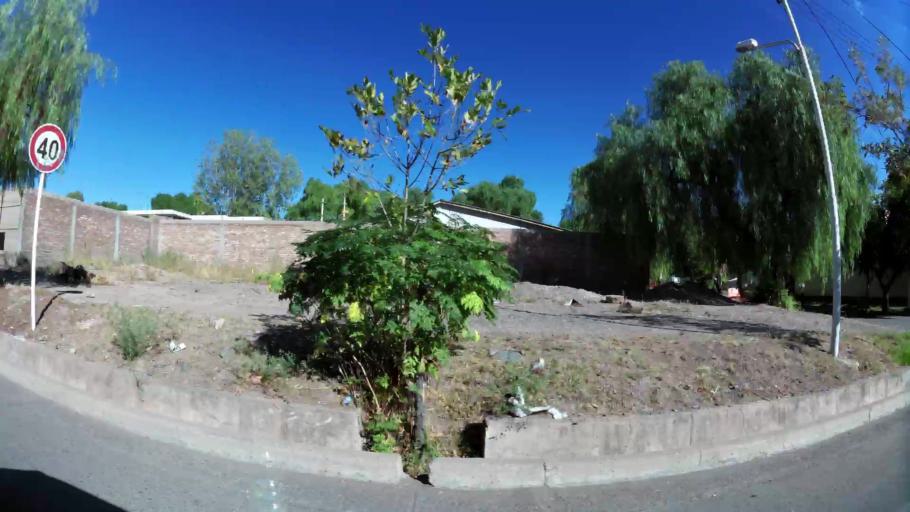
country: AR
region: Mendoza
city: Mendoza
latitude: -32.8779
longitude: -68.8734
